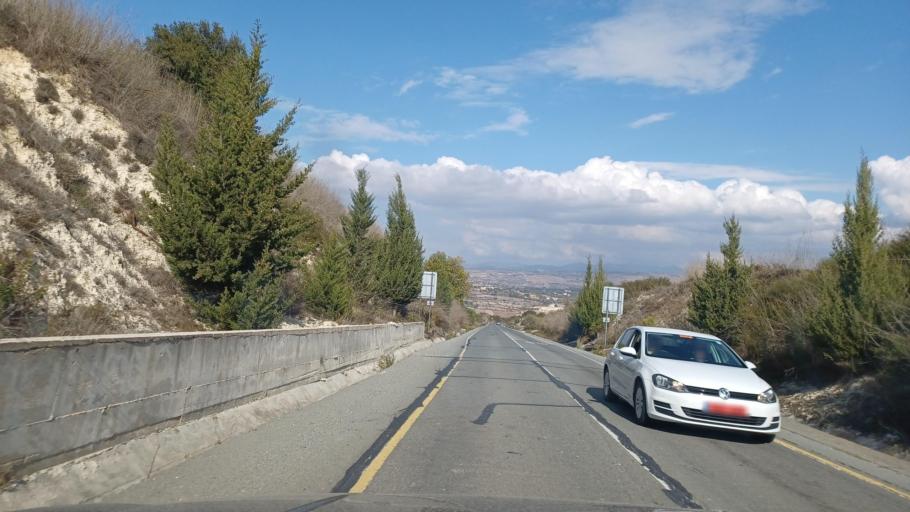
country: CY
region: Pafos
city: Mesogi
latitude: 34.8551
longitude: 32.4956
